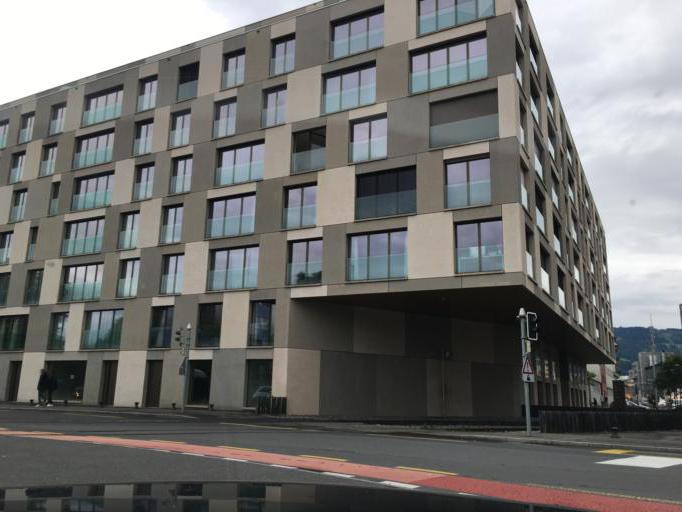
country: CH
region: Lucerne
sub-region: Lucerne-Stadt District
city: Luzern
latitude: 47.0475
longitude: 8.3143
